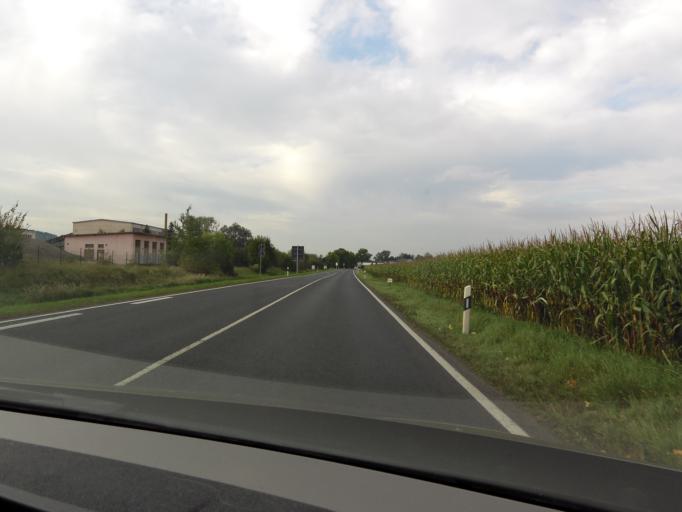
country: DE
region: Thuringia
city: Breitungen
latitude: 50.7688
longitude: 10.3197
